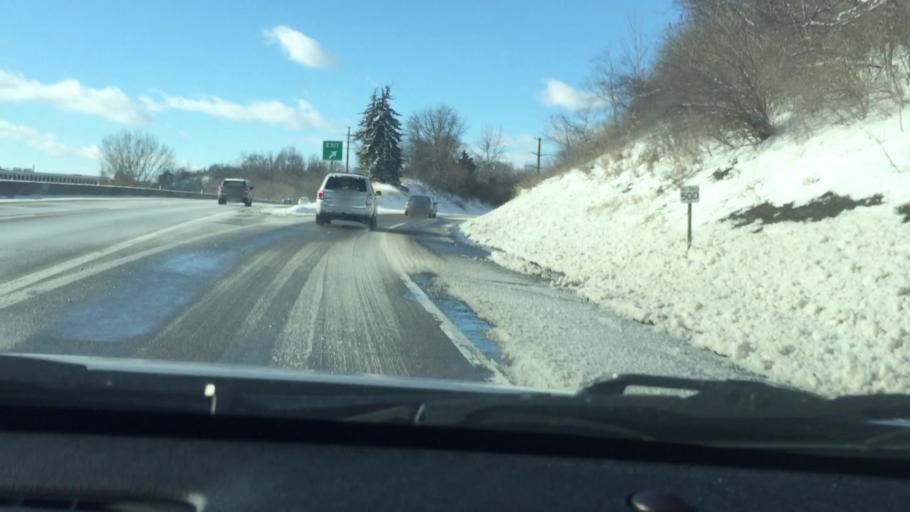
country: US
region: Pennsylvania
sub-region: Allegheny County
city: Oakdale
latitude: 40.4397
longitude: -80.1894
